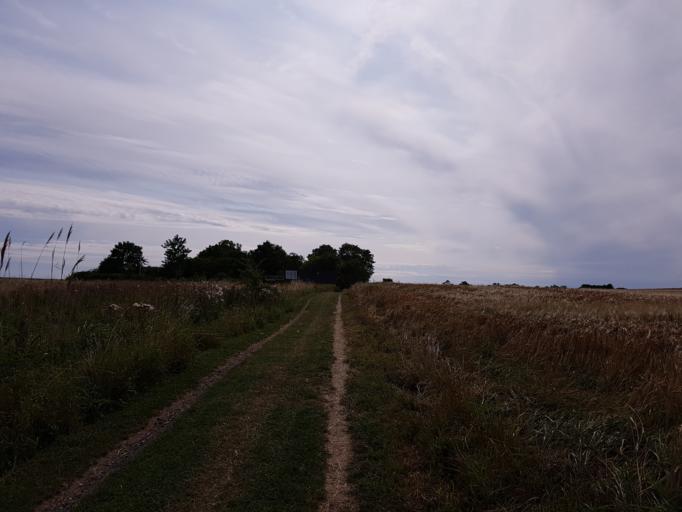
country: DK
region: Zealand
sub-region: Guldborgsund Kommune
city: Nykobing Falster
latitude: 54.5671
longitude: 11.9701
